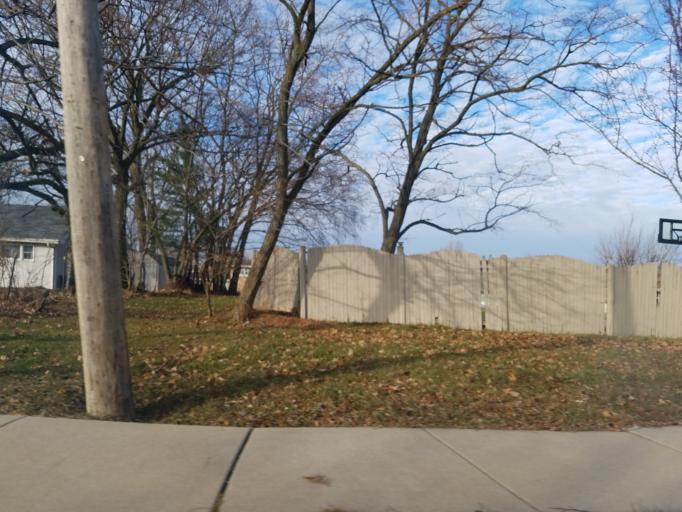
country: US
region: Illinois
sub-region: Will County
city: Mokena
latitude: 41.5262
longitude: -87.8779
